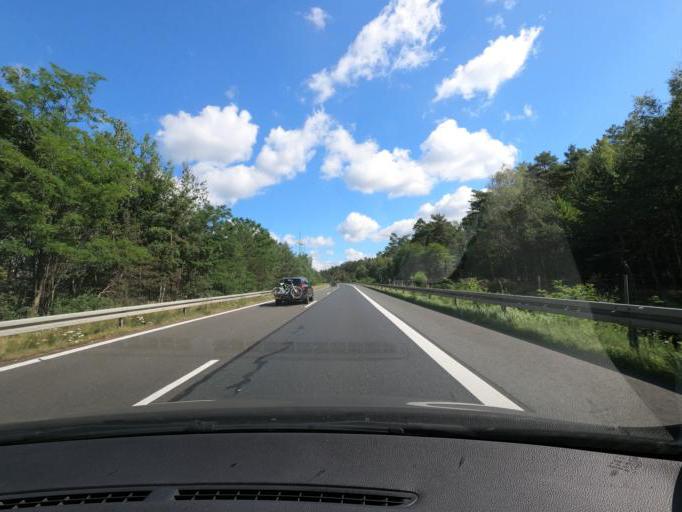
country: DE
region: Brandenburg
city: Fichtenwalde
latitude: 52.2837
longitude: 12.9150
